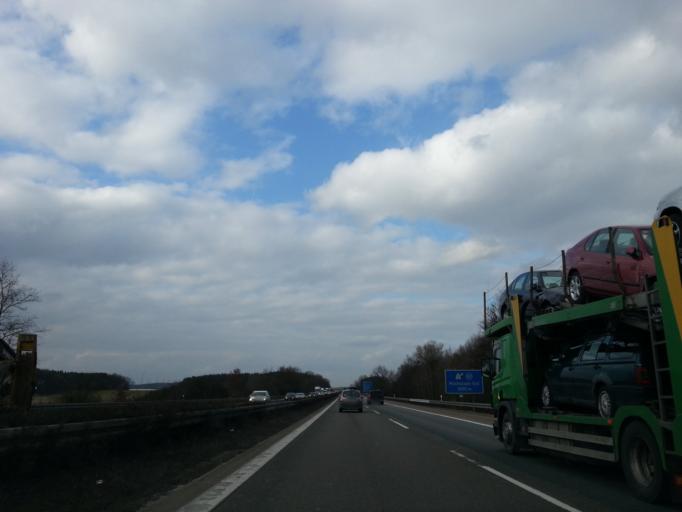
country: DE
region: Bavaria
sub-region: Regierungsbezirk Mittelfranken
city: Gremsdorf
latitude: 49.6899
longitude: 10.8602
